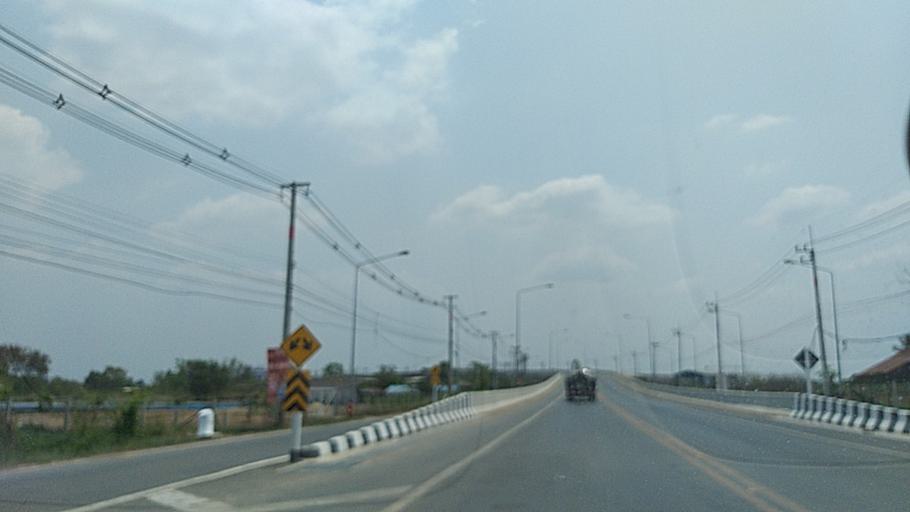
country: TH
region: Chachoengsao
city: Chachoengsao
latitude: 13.7477
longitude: 101.0785
